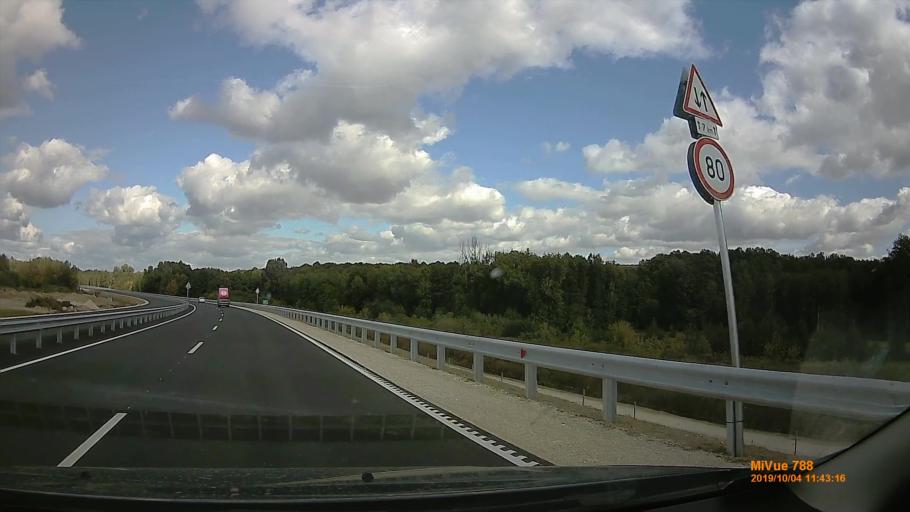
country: HU
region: Somogy
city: Karad
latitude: 46.5993
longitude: 17.8030
